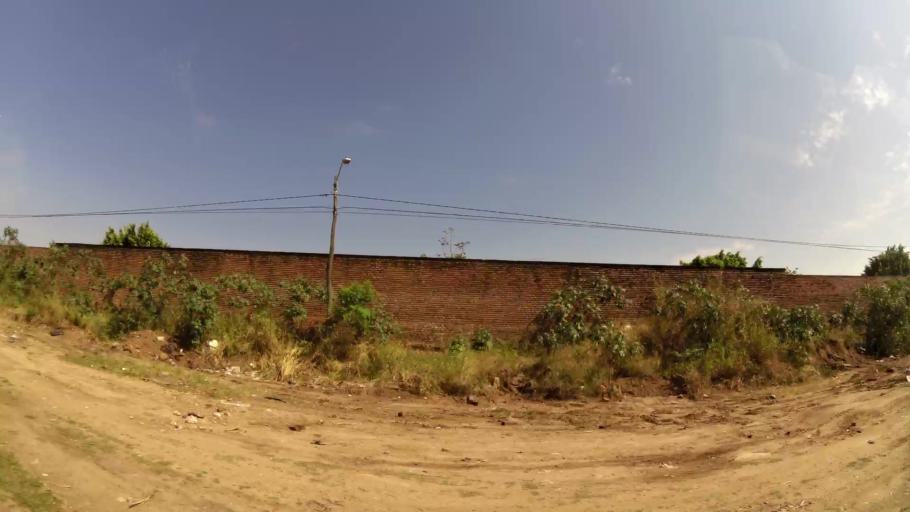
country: BO
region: Santa Cruz
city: Santa Cruz de la Sierra
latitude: -17.7488
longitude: -63.1596
